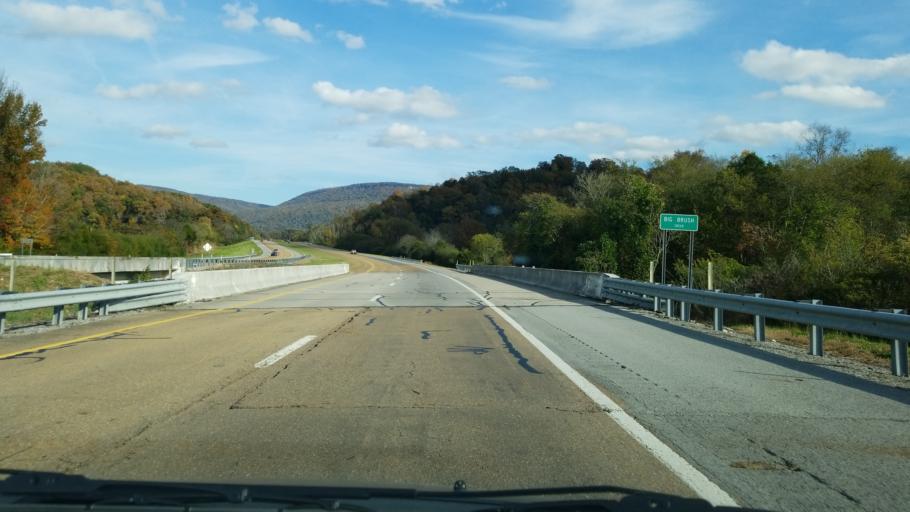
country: US
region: Tennessee
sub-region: Sequatchie County
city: Dunlap
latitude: 35.3927
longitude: -85.3658
